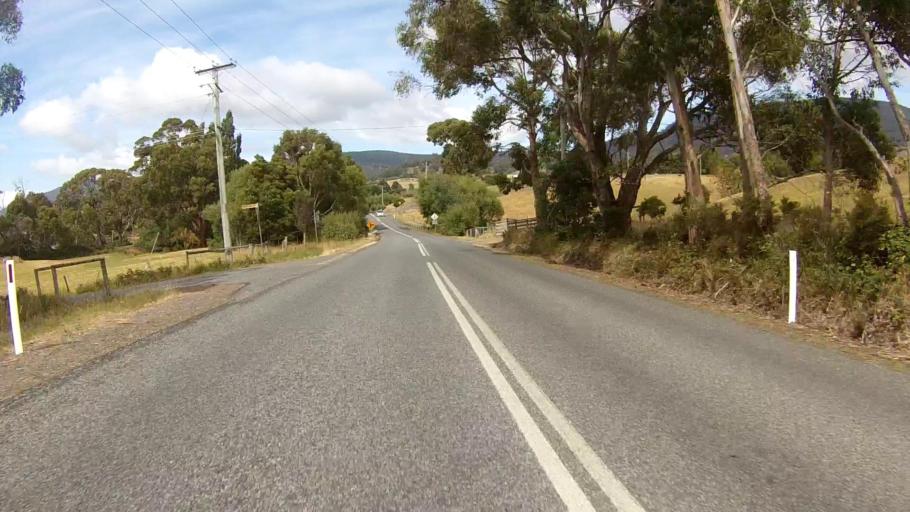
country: AU
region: Tasmania
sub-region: Kingborough
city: Kettering
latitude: -43.1519
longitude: 147.2396
